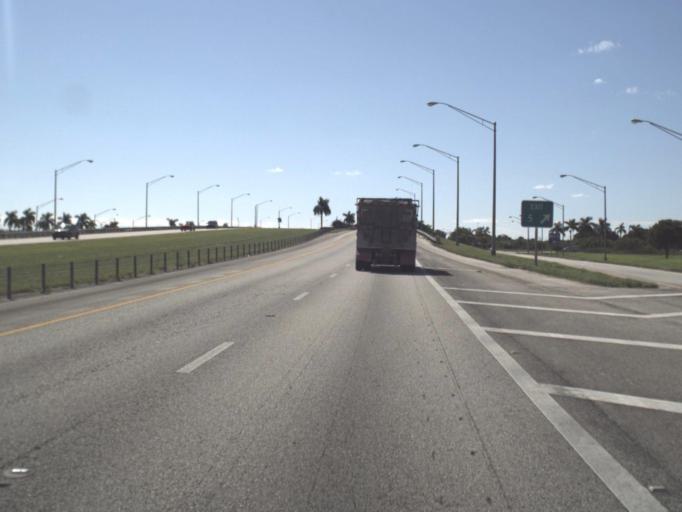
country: US
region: Florida
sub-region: Miami-Dade County
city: Leisure City
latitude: 25.5030
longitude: -80.4174
